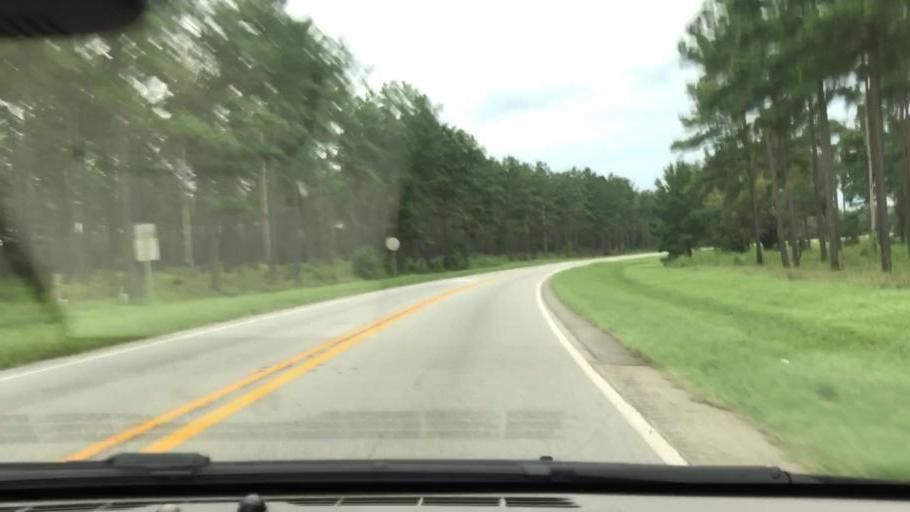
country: US
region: Georgia
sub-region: Early County
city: Blakely
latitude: 31.2823
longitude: -85.0711
